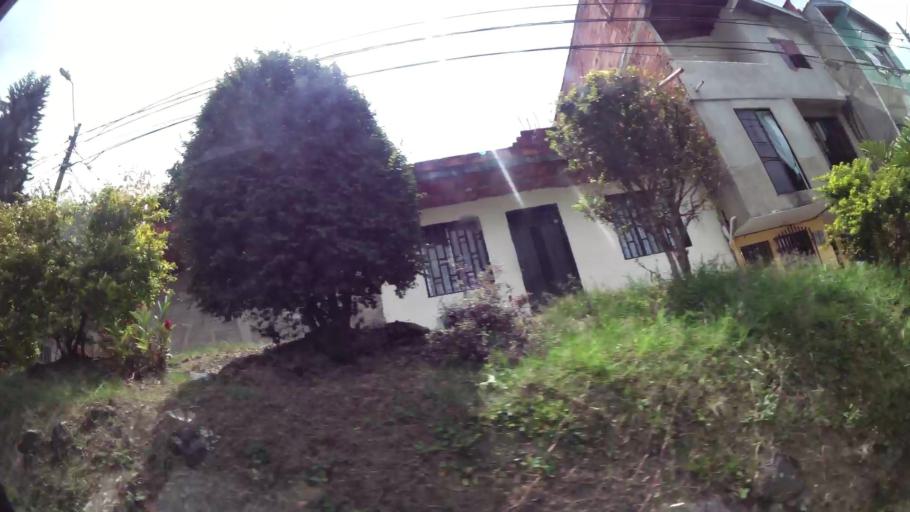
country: CO
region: Antioquia
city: Municipio de Copacabana
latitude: 6.3429
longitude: -75.5058
